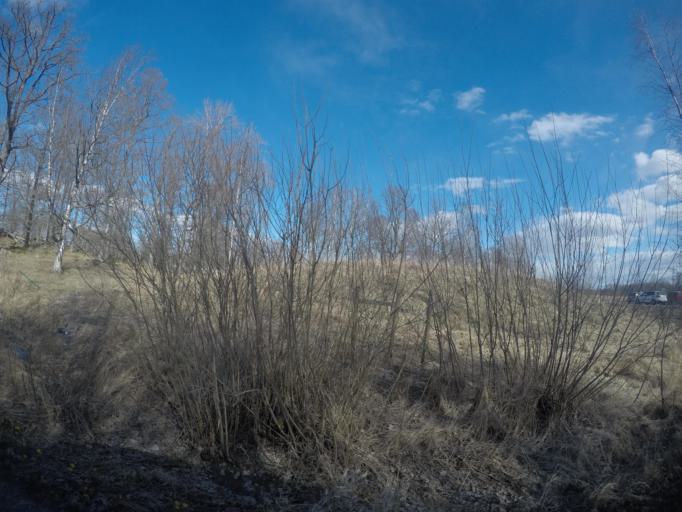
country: SE
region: OErebro
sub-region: Orebro Kommun
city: Hovsta
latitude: 59.3050
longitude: 15.2789
